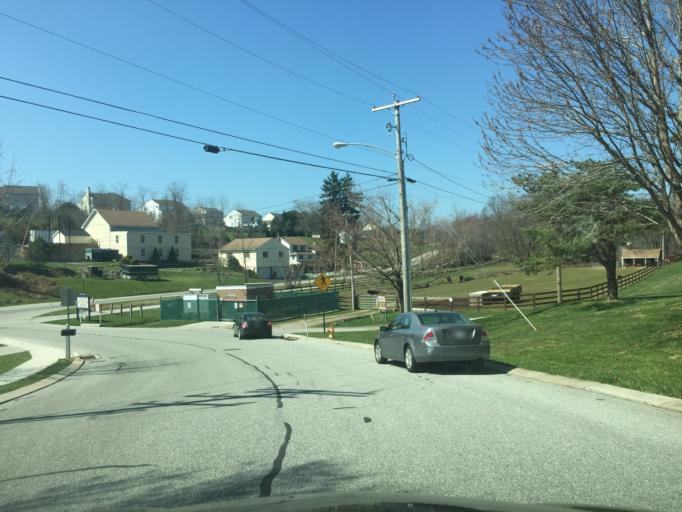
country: US
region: Pennsylvania
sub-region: York County
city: New Freedom
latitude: 39.7222
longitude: -76.6975
